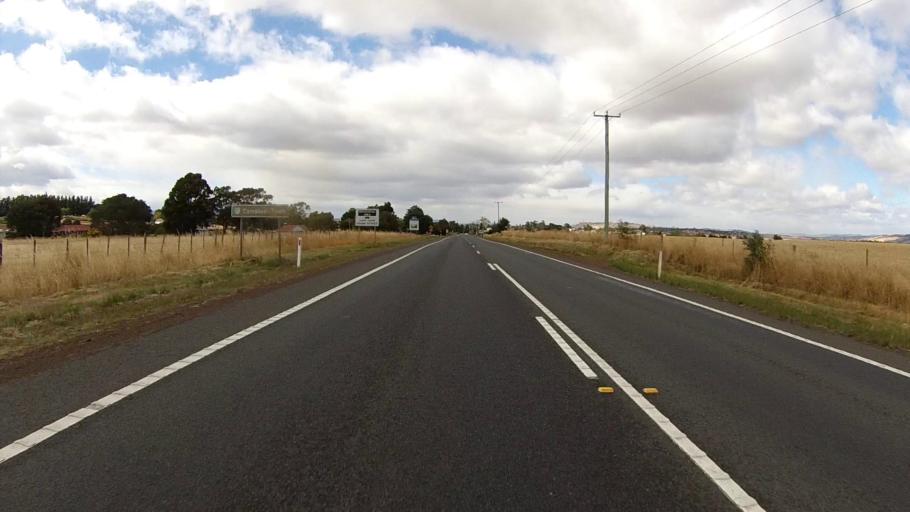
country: AU
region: Tasmania
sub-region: Northern Midlands
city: Evandale
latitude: -41.9124
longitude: 147.4825
